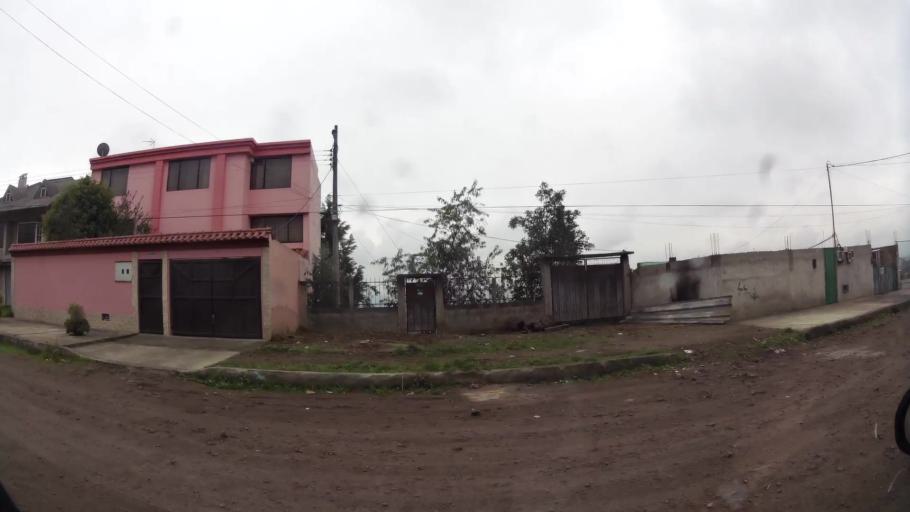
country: EC
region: Pichincha
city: Sangolqui
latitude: -0.2763
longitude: -78.4748
